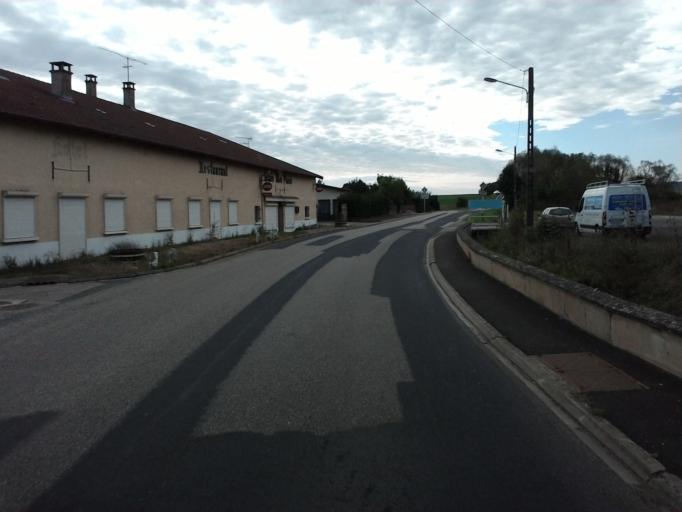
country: FR
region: Lorraine
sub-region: Departement de Meurthe-et-Moselle
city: Ecrouves
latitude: 48.7644
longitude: 5.8641
